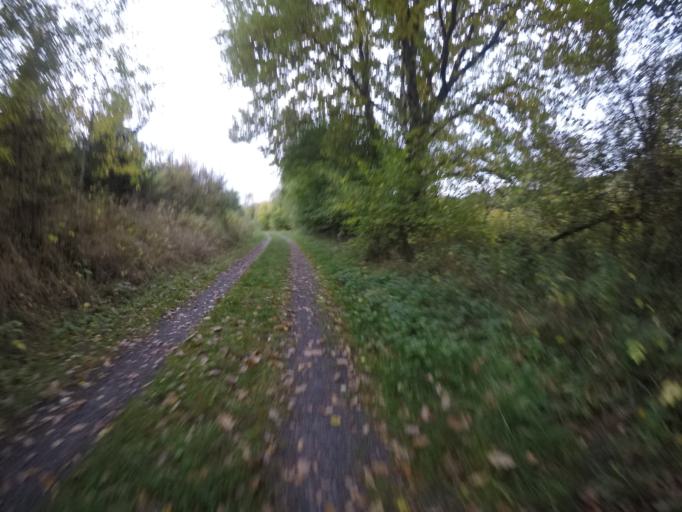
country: BE
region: Wallonia
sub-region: Province du Luxembourg
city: Fauvillers
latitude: 49.8508
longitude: 5.6974
